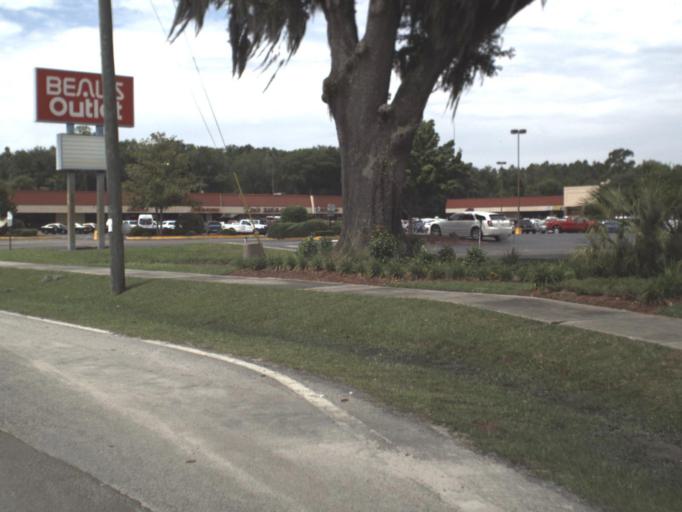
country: US
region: Florida
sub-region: Suwannee County
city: Live Oak
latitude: 30.2826
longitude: -82.9878
